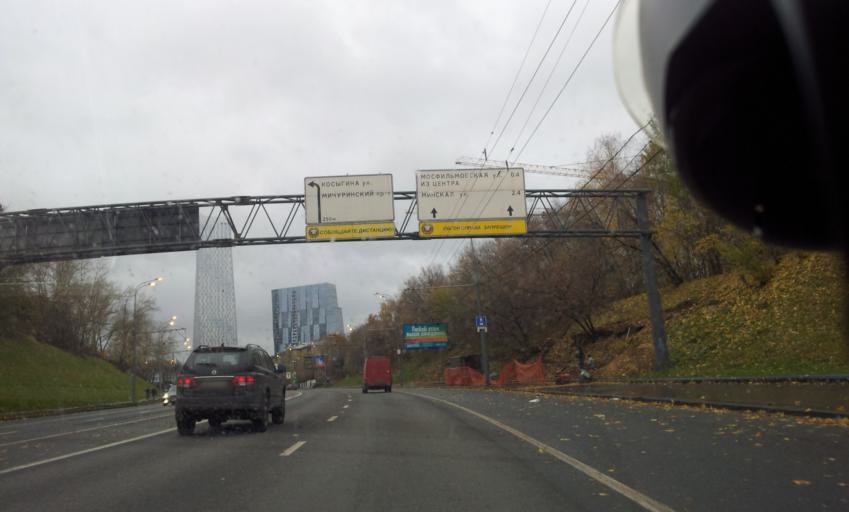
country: RU
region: Moscow
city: Vorob'yovo
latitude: 55.7281
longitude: 37.5396
